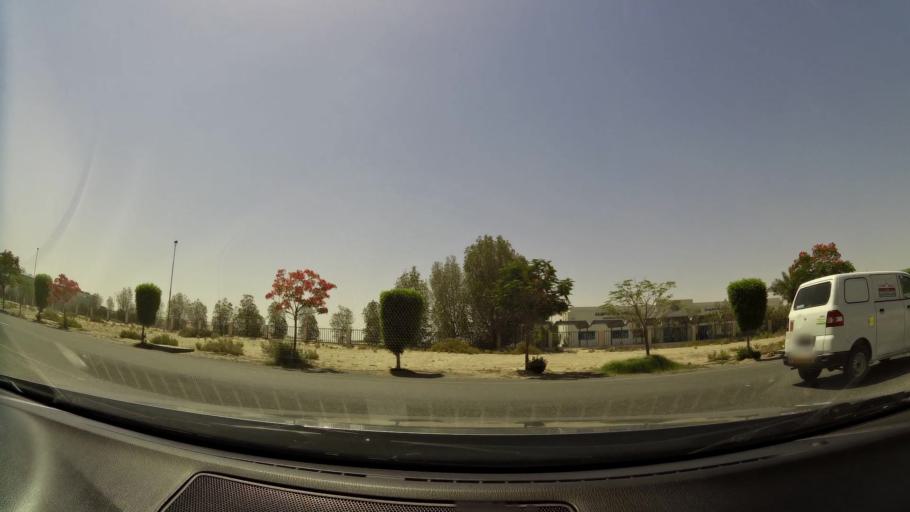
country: AE
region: Dubai
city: Dubai
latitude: 24.9819
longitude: 55.2115
